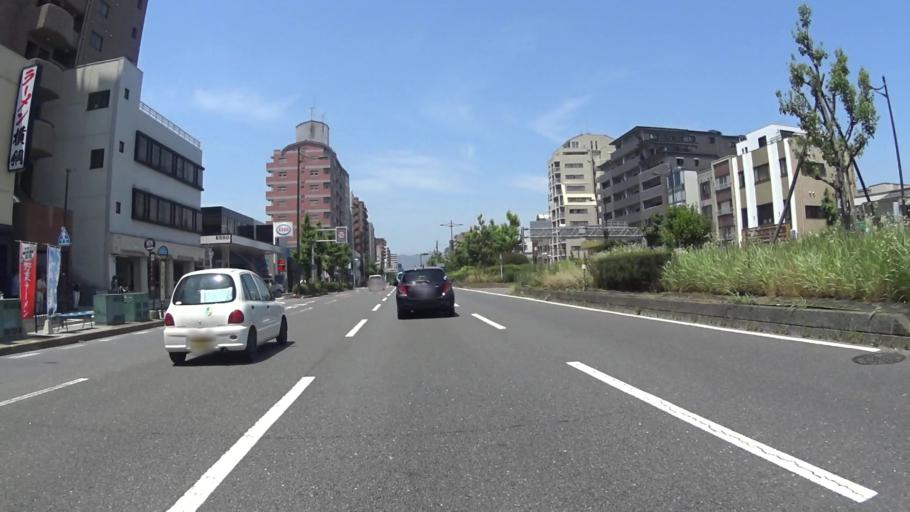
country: JP
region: Kyoto
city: Kyoto
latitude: 34.9962
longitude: 135.7482
